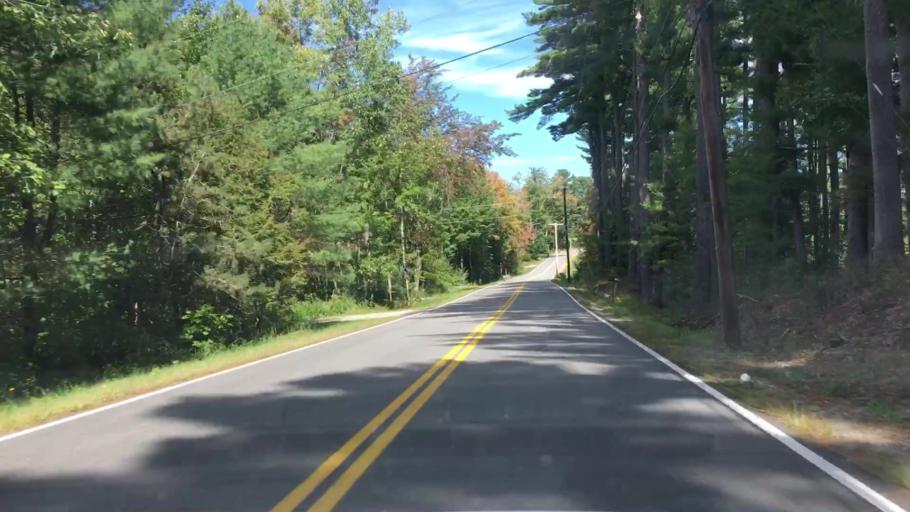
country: US
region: Maine
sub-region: York County
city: Saco
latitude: 43.5666
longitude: -70.4840
